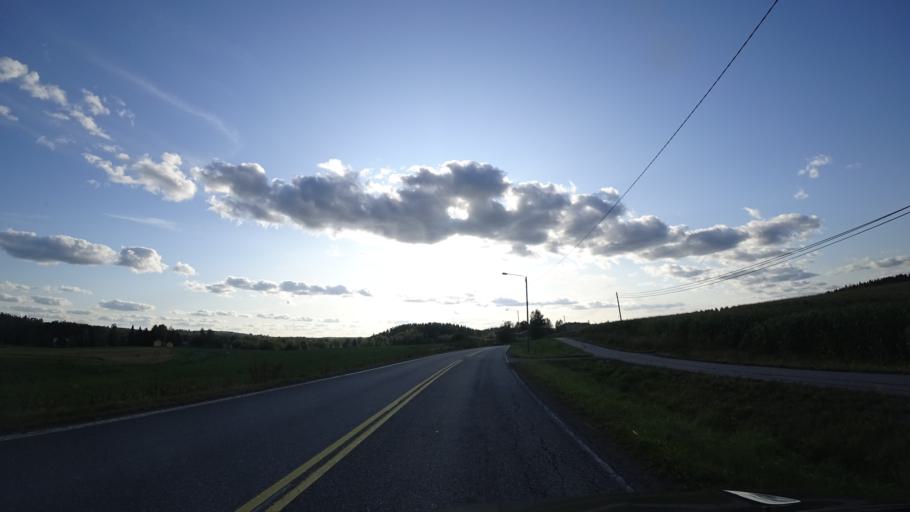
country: FI
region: Haeme
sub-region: Haemeenlinna
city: Lammi
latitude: 61.0807
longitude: 25.0412
